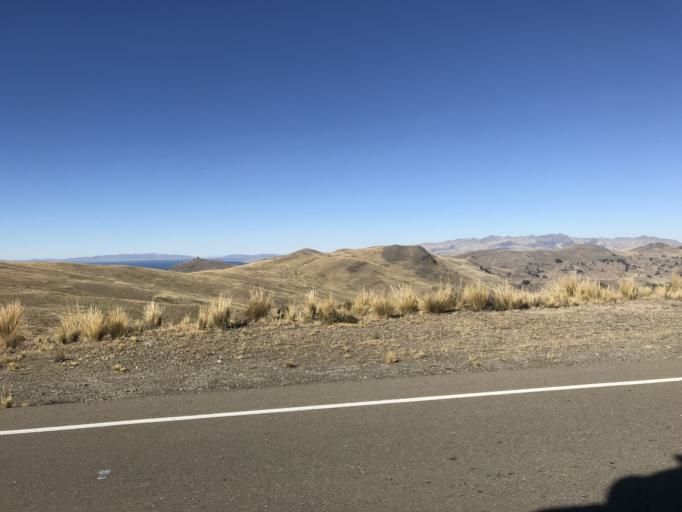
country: PE
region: Puno
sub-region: Yunguyo
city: Yunguyo
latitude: -16.1589
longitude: -68.9923
